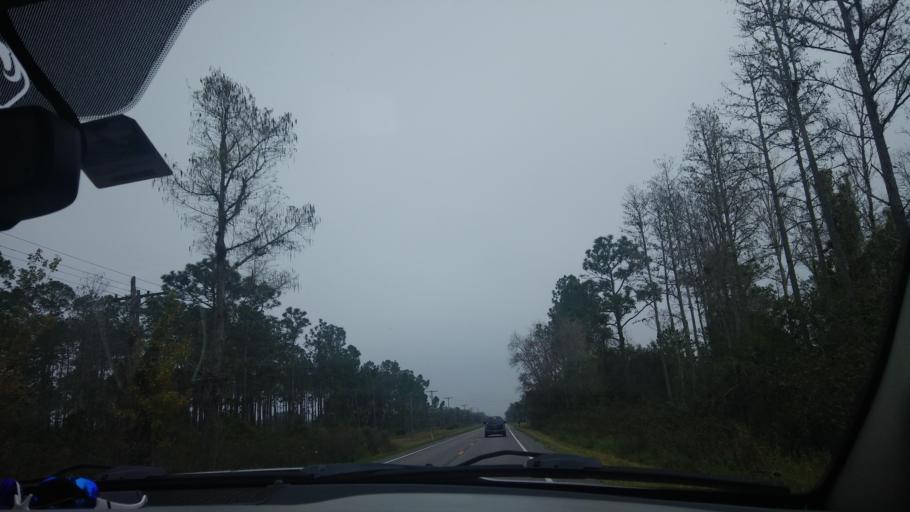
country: US
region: Florida
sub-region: Brevard County
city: June Park
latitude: 27.9182
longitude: -80.9960
